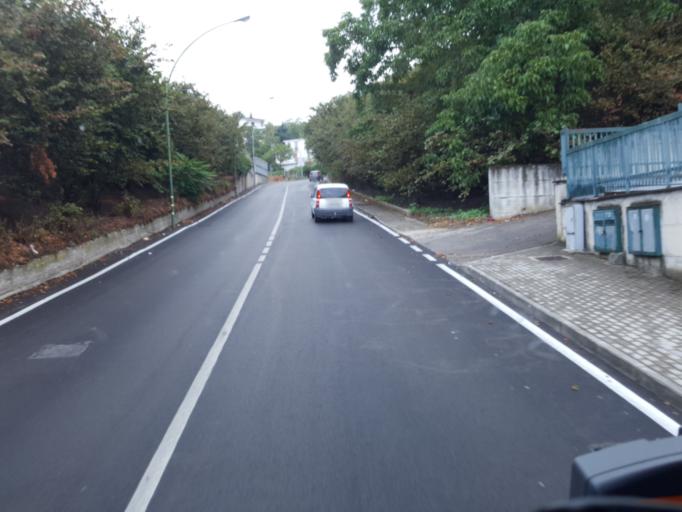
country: IT
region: Campania
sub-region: Provincia di Napoli
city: Carbonara di Nola
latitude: 40.8788
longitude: 14.5818
